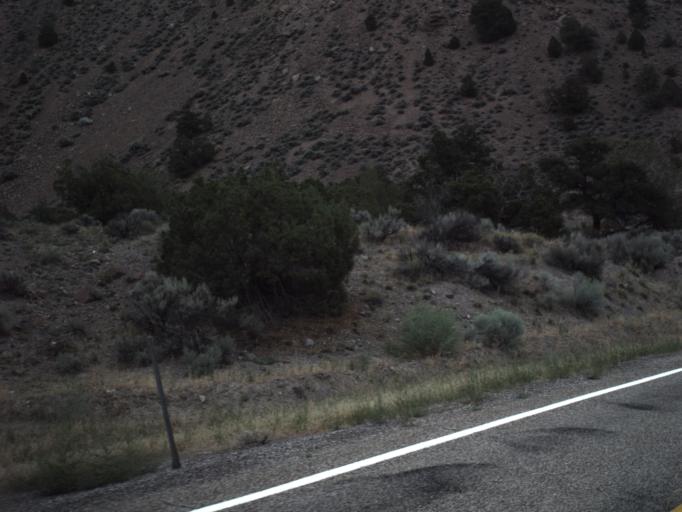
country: US
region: Utah
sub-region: Piute County
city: Junction
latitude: 38.1948
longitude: -112.1355
